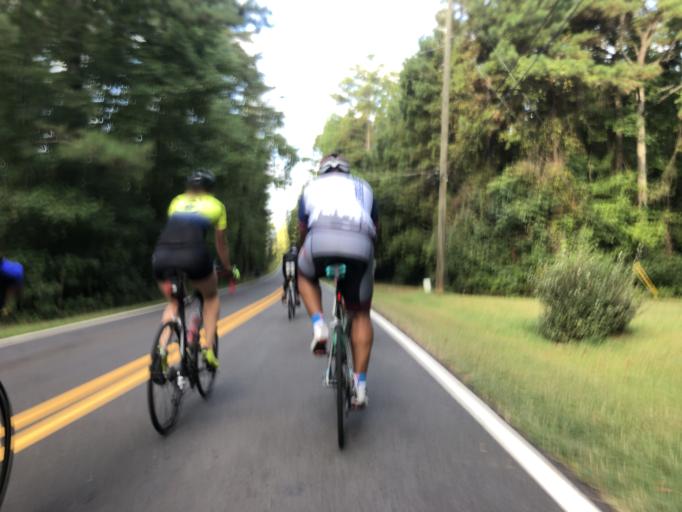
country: US
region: Georgia
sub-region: Fulton County
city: Palmetto
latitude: 33.5738
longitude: -84.6599
